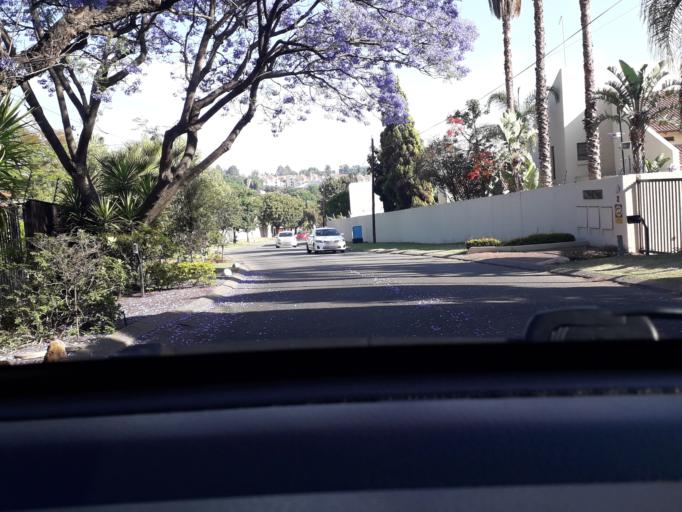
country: ZA
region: Gauteng
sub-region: City of Johannesburg Metropolitan Municipality
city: Modderfontein
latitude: -26.0701
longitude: 28.0654
